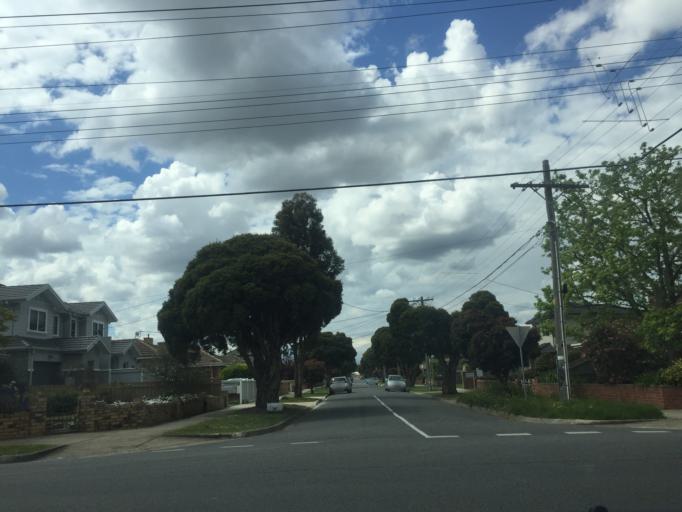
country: AU
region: Victoria
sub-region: Darebin
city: Reservoir
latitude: -37.7138
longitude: 145.0126
